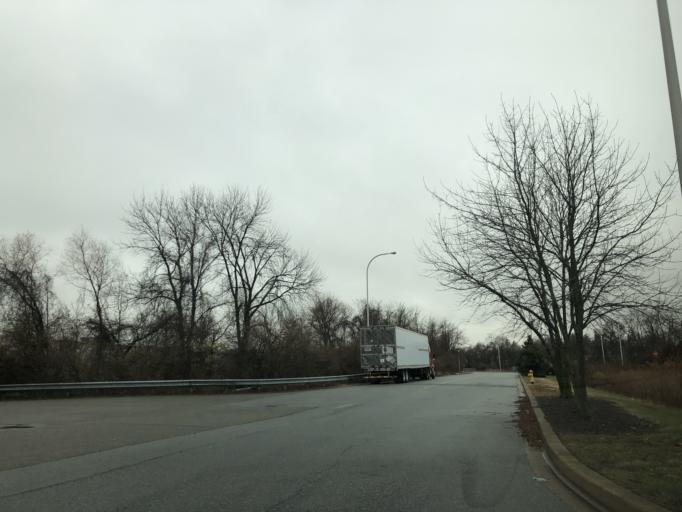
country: US
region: Delaware
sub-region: New Castle County
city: Wilmington Manor
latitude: 39.7151
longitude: -75.5638
